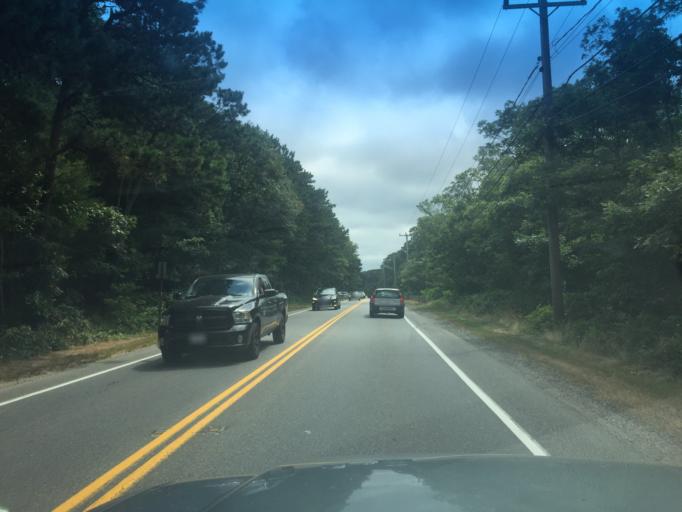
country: US
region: Massachusetts
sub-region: Barnstable County
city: East Falmouth
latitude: 41.6165
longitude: -70.5275
